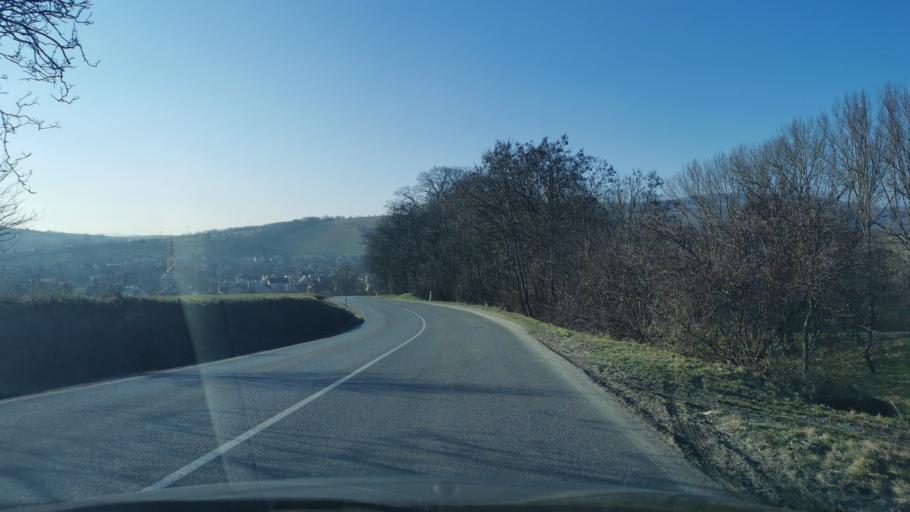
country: SK
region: Trnavsky
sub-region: Okres Senica
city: Senica
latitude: 48.7321
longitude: 17.4166
